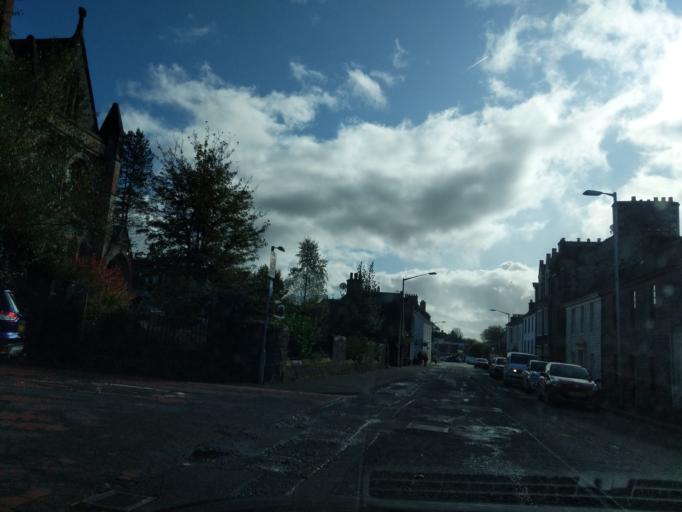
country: GB
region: Scotland
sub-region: Dumfries and Galloway
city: Moffat
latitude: 55.3356
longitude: -3.4456
